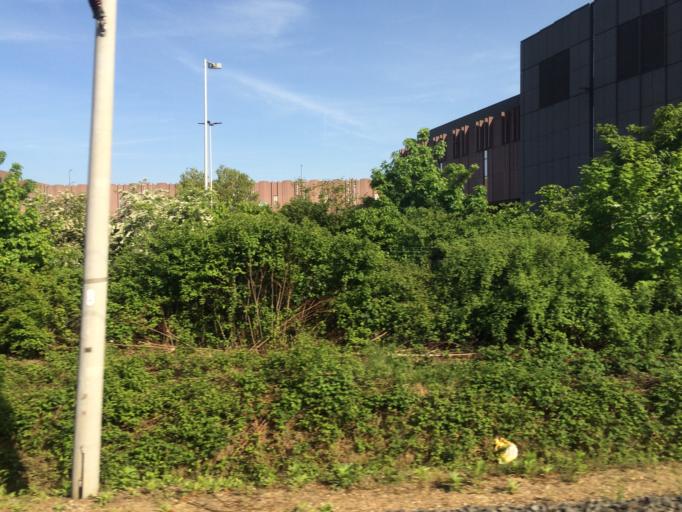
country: DE
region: North Rhine-Westphalia
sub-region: Regierungsbezirk Koln
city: Deutz
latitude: 50.9444
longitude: 6.9742
